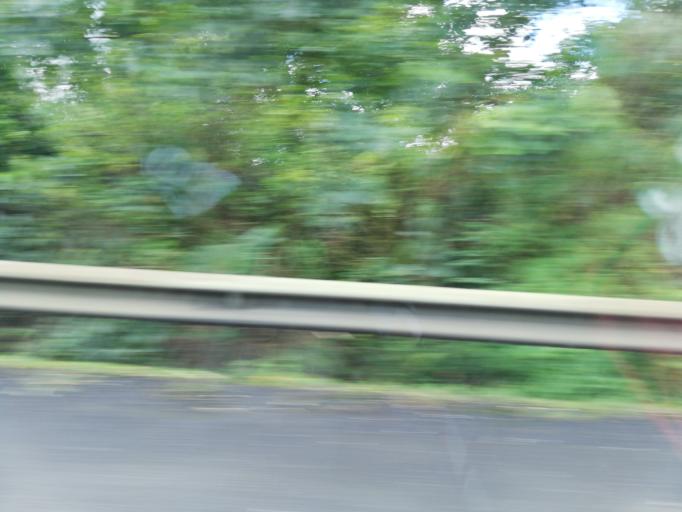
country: MU
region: Grand Port
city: Nouvelle France
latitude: -20.3512
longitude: 57.5721
